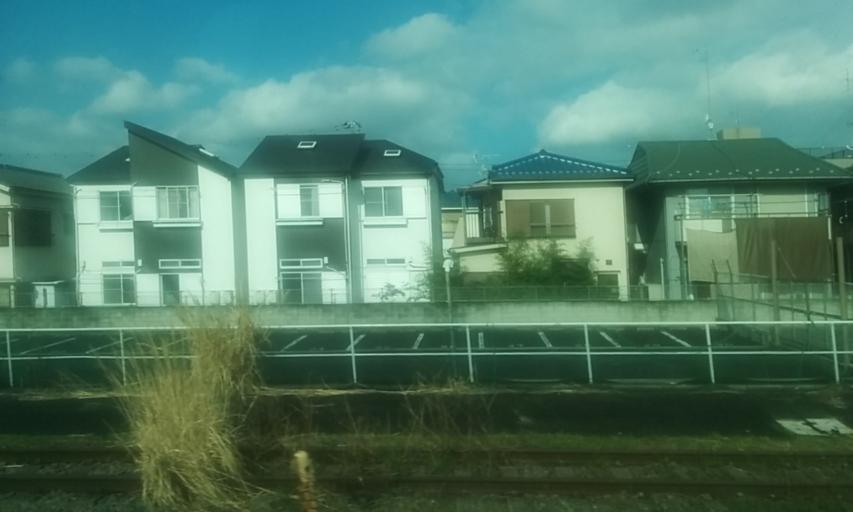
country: JP
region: Kanagawa
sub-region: Kawasaki-shi
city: Kawasaki
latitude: 35.5143
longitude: 139.6778
